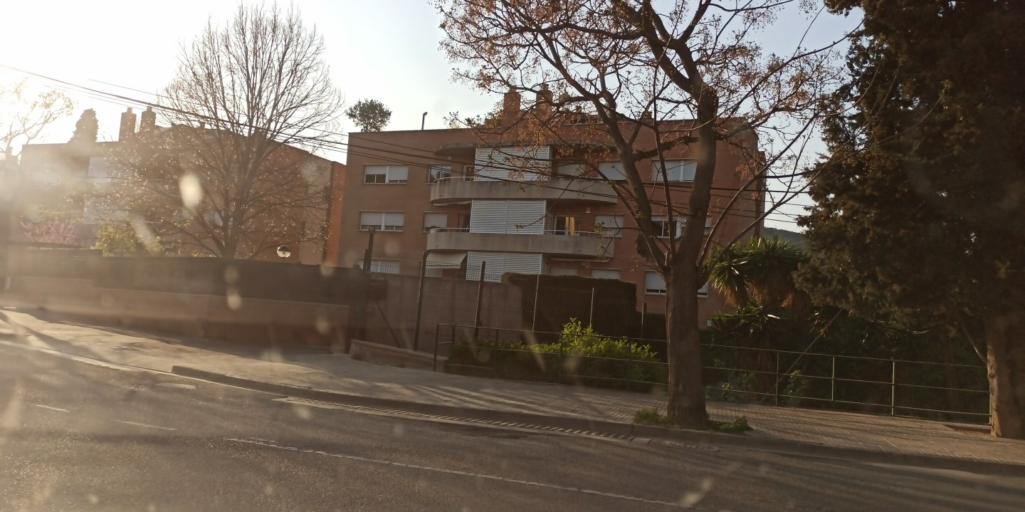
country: ES
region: Catalonia
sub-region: Provincia de Barcelona
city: Sant Just Desvern
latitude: 41.3883
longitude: 2.0777
